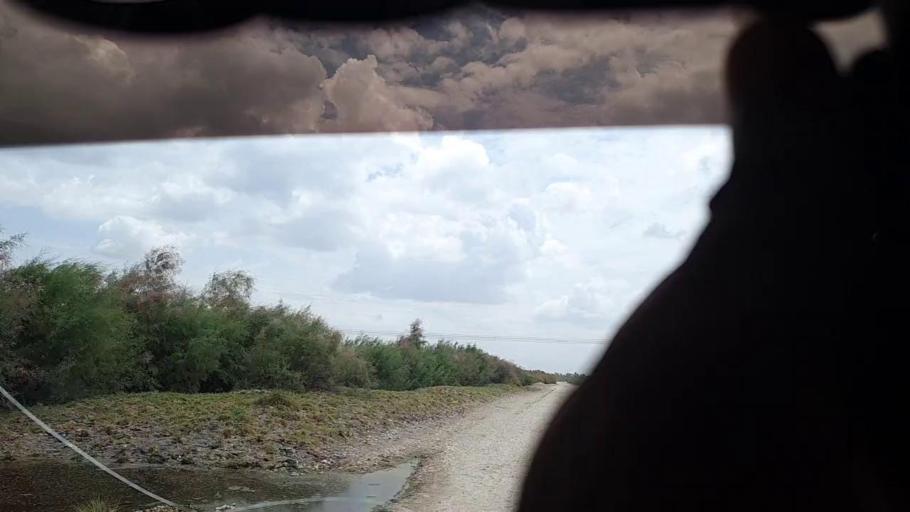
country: PK
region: Sindh
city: Ghauspur
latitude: 28.0669
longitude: 68.9386
